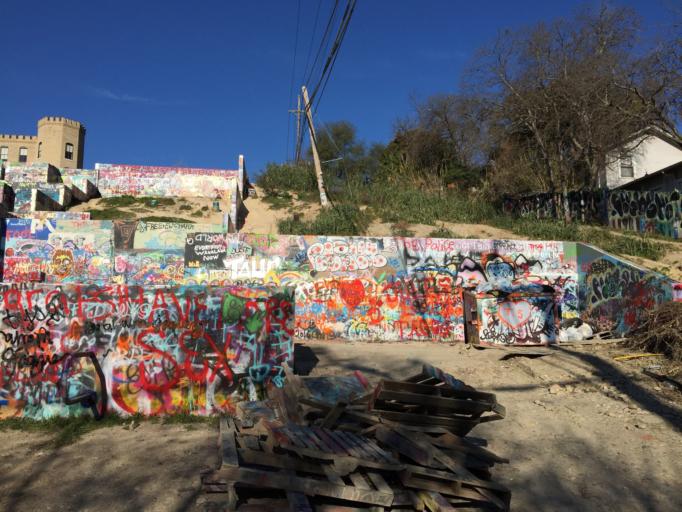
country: US
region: Texas
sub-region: Travis County
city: Austin
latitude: 30.2763
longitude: -97.7529
